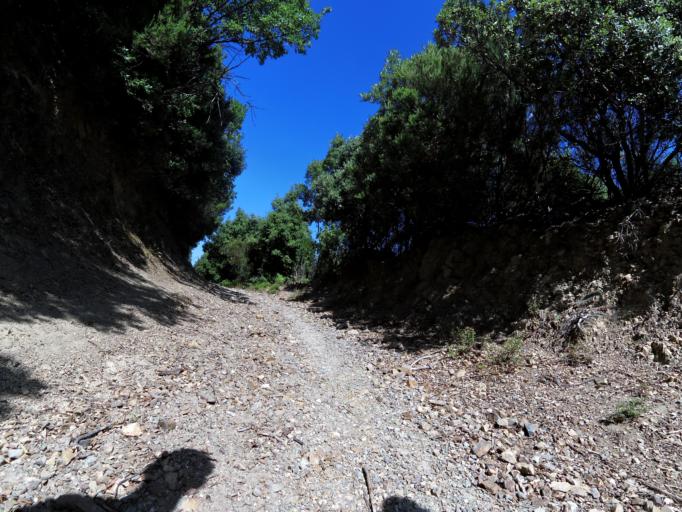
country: IT
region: Calabria
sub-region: Provincia di Reggio Calabria
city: Bivongi
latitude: 38.5031
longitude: 16.4424
